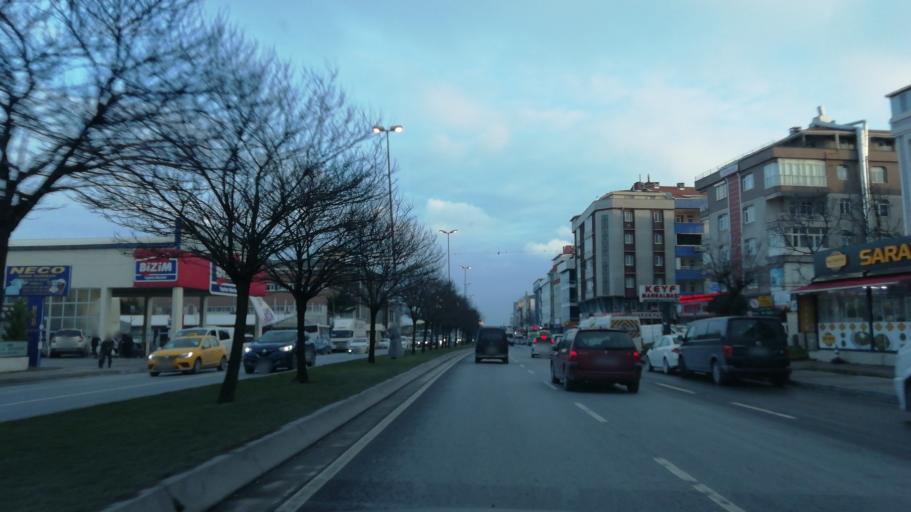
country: TR
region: Istanbul
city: Yakuplu
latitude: 41.0046
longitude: 28.7078
